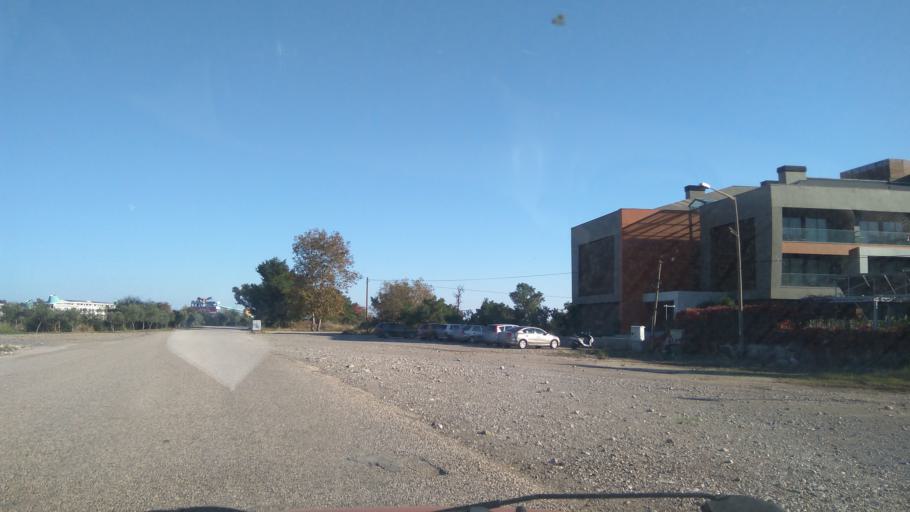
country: TR
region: Antalya
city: Kemer
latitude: 36.5664
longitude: 30.5670
